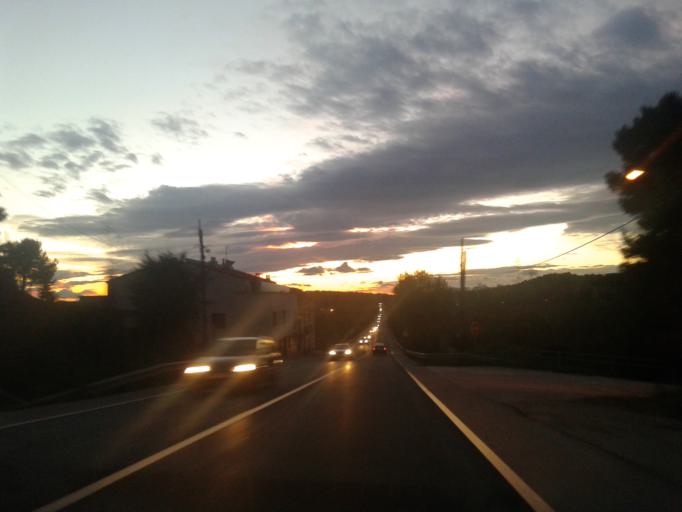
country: ES
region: Catalonia
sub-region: Provincia de Barcelona
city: Subirats
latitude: 41.3949
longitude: 1.8452
